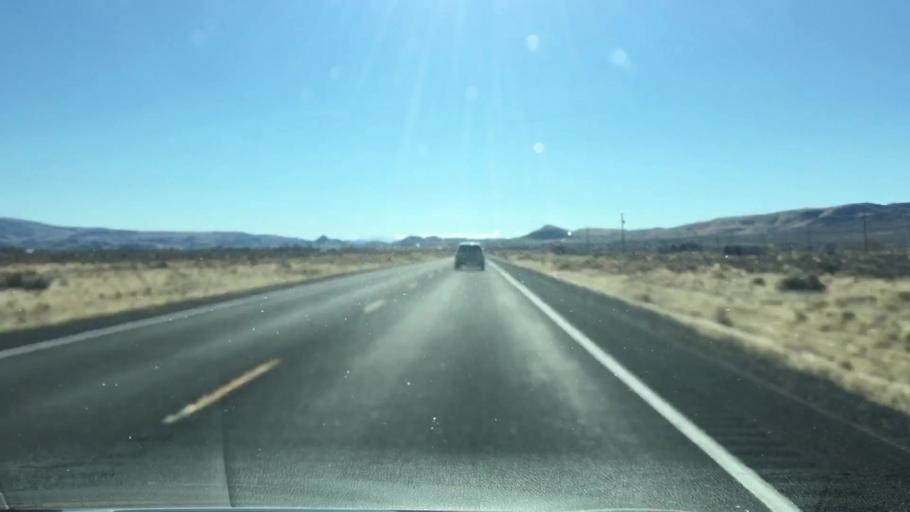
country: US
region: Nevada
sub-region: Lyon County
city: Silver Springs
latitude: 39.3857
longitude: -119.2317
